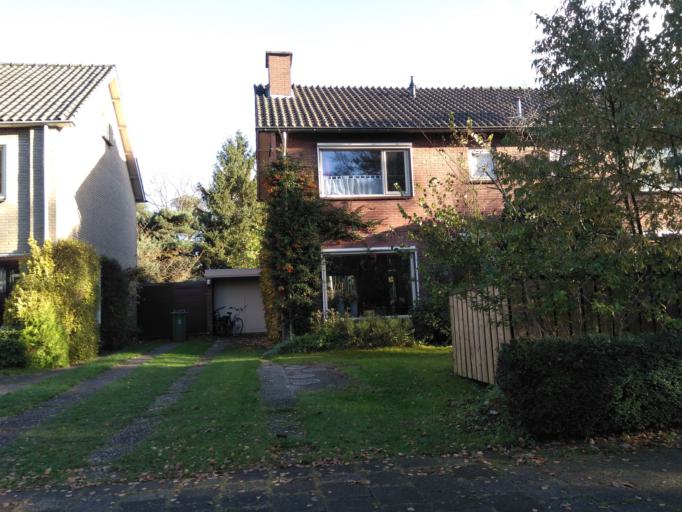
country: NL
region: Gelderland
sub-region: Gemeente Ede
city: Ede
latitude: 52.0335
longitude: 5.6642
